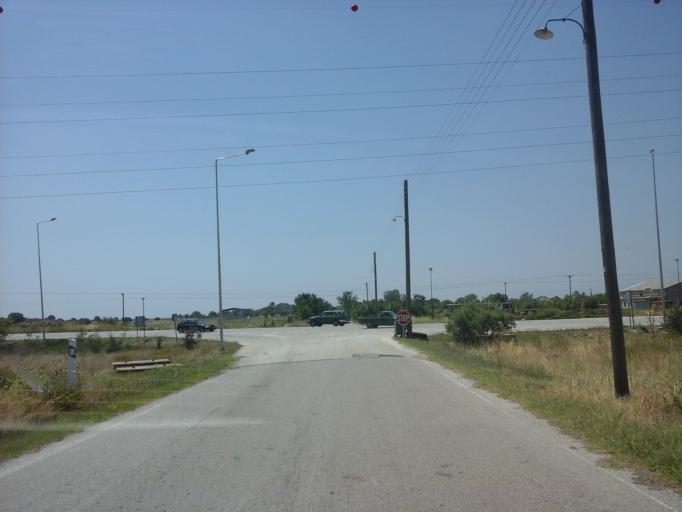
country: GR
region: East Macedonia and Thrace
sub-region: Nomos Evrou
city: Feres
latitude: 40.8622
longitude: 26.0334
